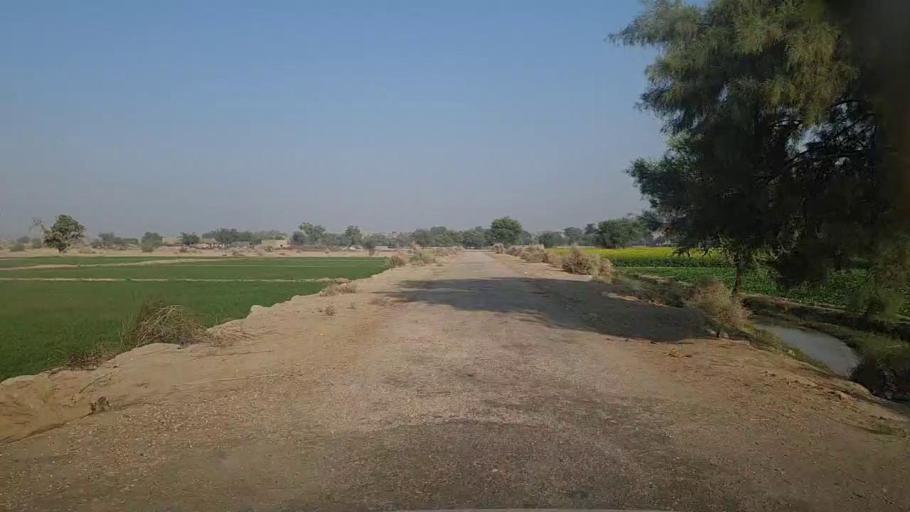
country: PK
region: Sindh
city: Kandiari
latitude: 26.7677
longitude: 68.5077
